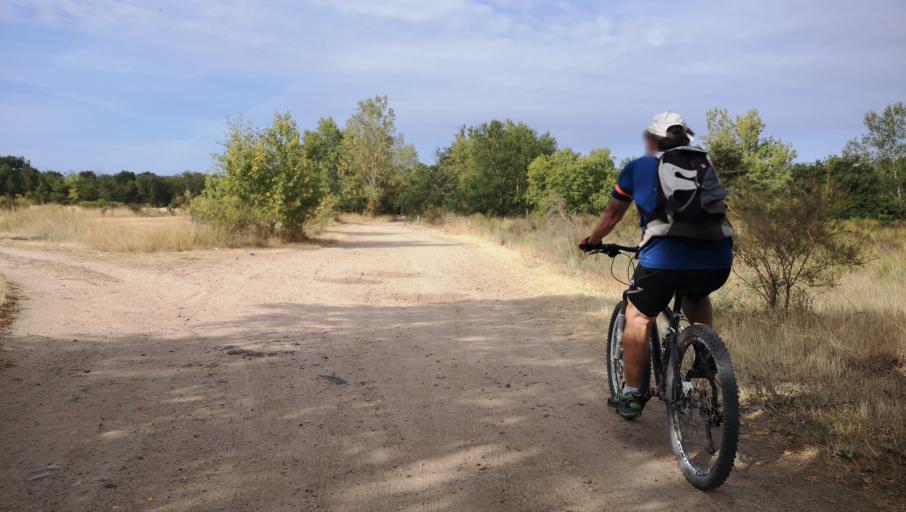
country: FR
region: Centre
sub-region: Departement du Loiret
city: Sandillon
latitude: 47.8617
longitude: 2.0378
